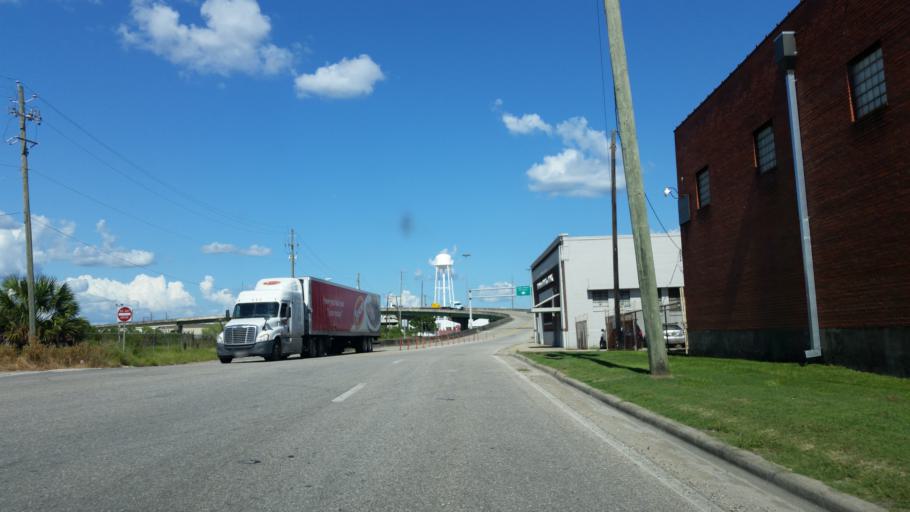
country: US
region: Alabama
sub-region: Mobile County
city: Mobile
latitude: 30.7003
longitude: -88.0443
